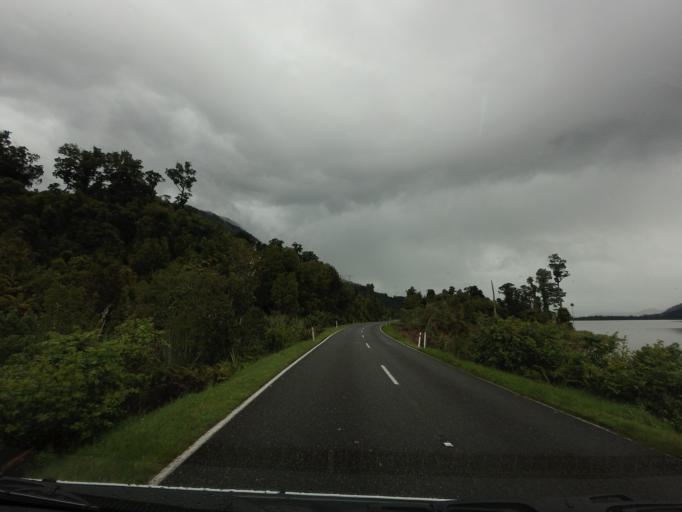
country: NZ
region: West Coast
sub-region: Westland District
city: Hokitika
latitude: -43.0510
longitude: 170.6378
